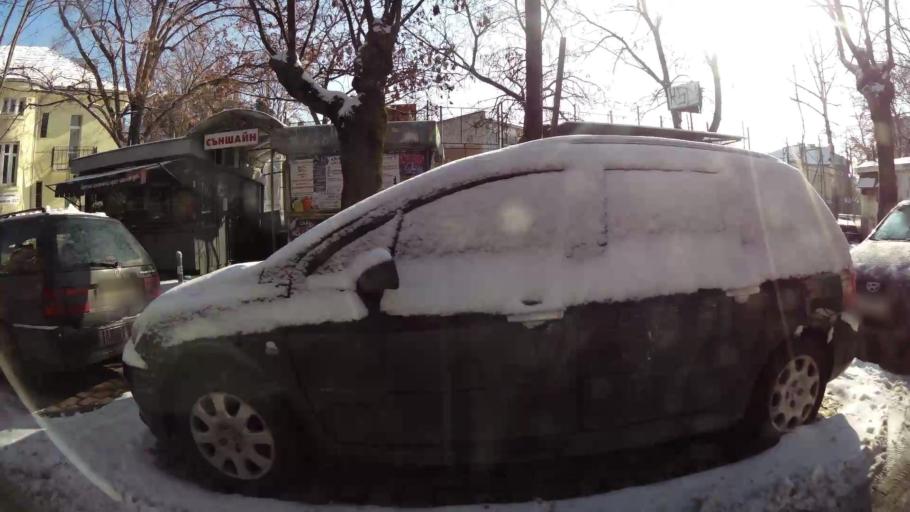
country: BG
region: Sofia-Capital
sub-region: Stolichna Obshtina
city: Sofia
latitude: 42.6829
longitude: 23.3282
